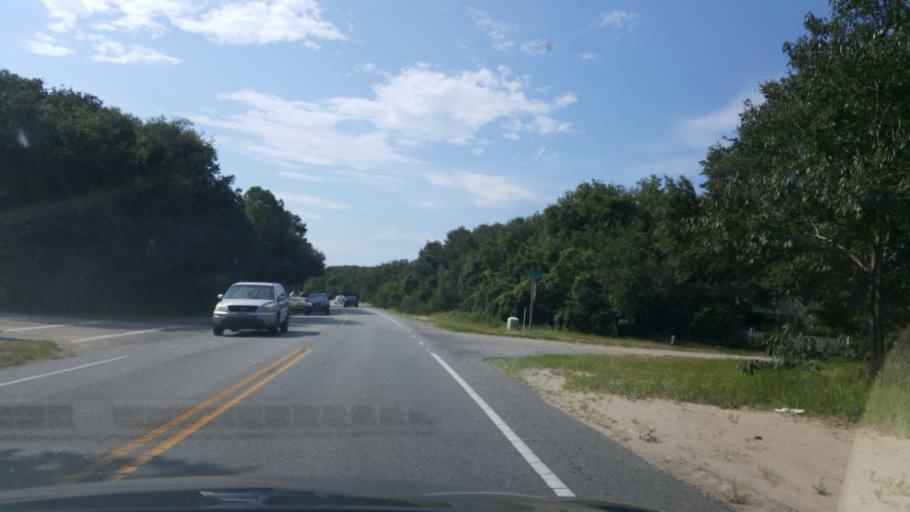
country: US
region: North Carolina
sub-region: Dare County
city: Southern Shores
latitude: 36.1467
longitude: -75.7412
